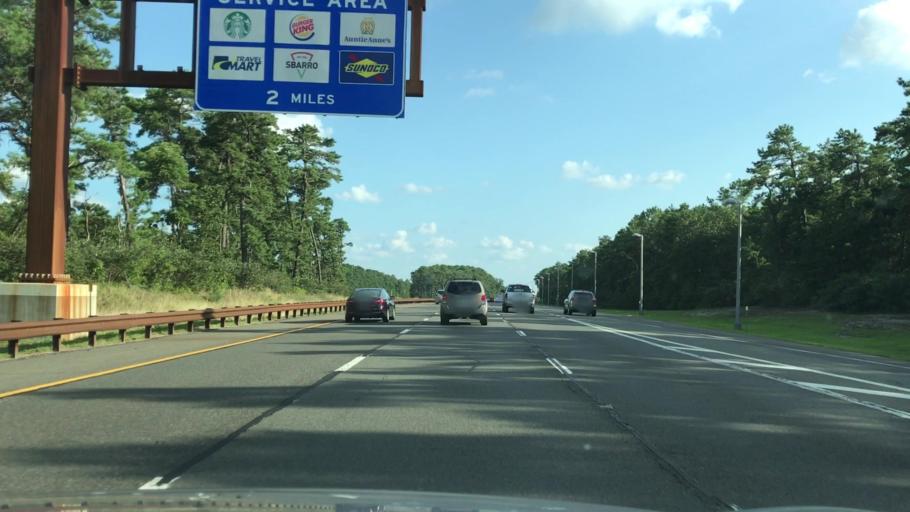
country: US
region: New Jersey
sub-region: Ocean County
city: South Toms River
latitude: 39.9033
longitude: -74.2122
